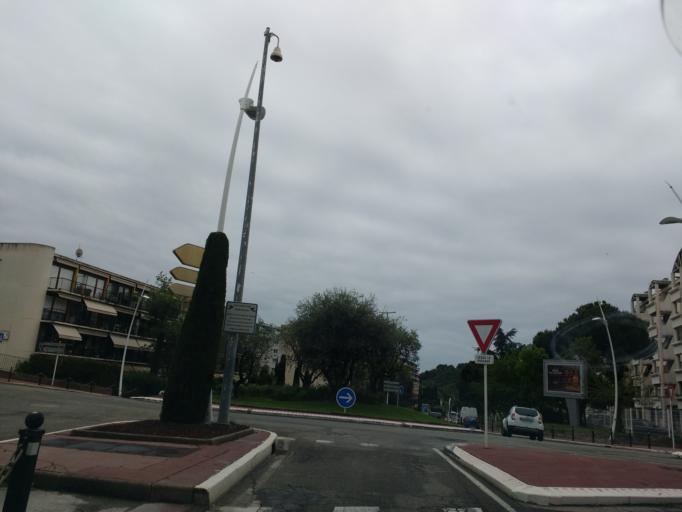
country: FR
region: Provence-Alpes-Cote d'Azur
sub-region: Departement des Alpes-Maritimes
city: Cannes
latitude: 43.5660
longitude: 7.0026
